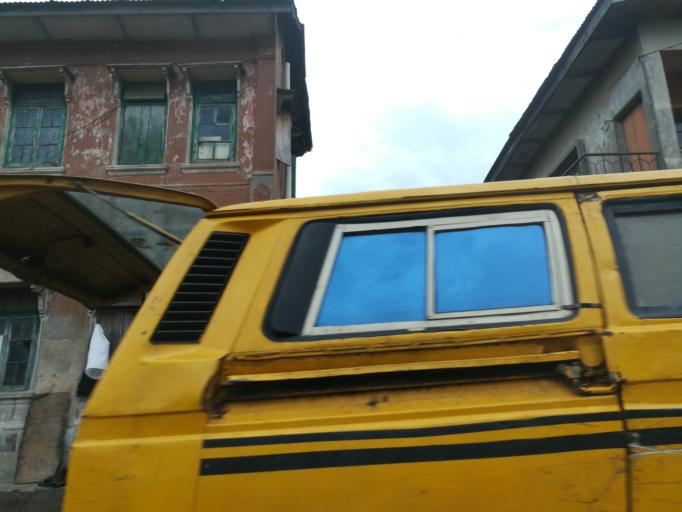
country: NG
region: Lagos
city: Ebute Metta
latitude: 6.4875
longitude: 3.3870
